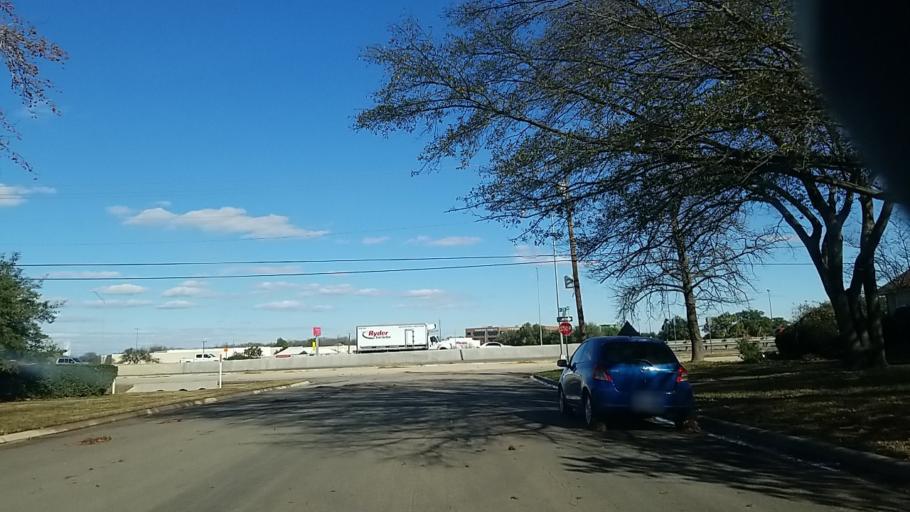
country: US
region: Texas
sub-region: Denton County
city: Denton
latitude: 33.1893
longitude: -97.1132
